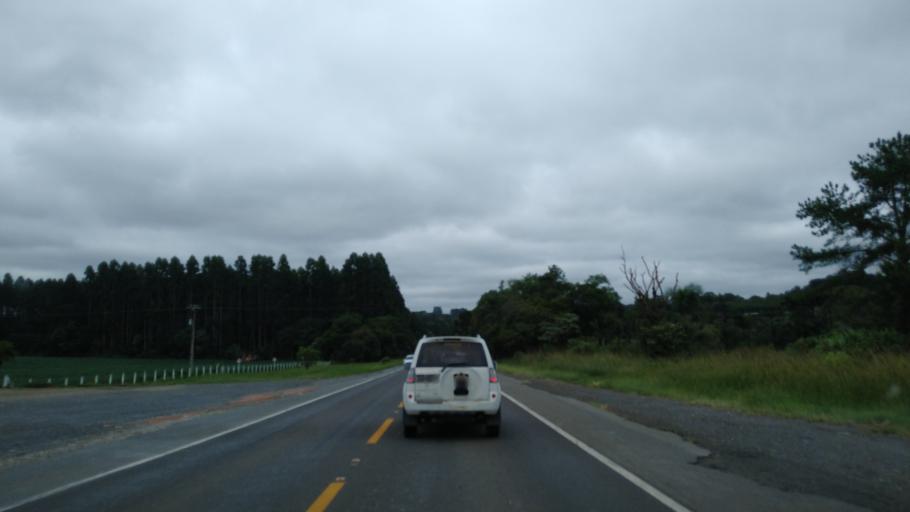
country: BR
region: Santa Catarina
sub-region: Tres Barras
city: Tres Barras
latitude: -26.1817
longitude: -50.2007
